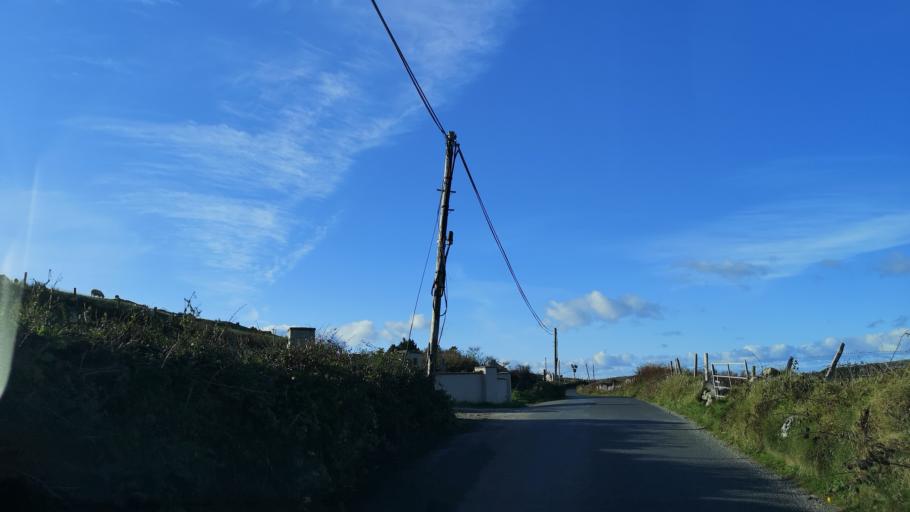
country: IE
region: Connaught
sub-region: County Galway
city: Clifden
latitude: 53.5077
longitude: -10.0904
